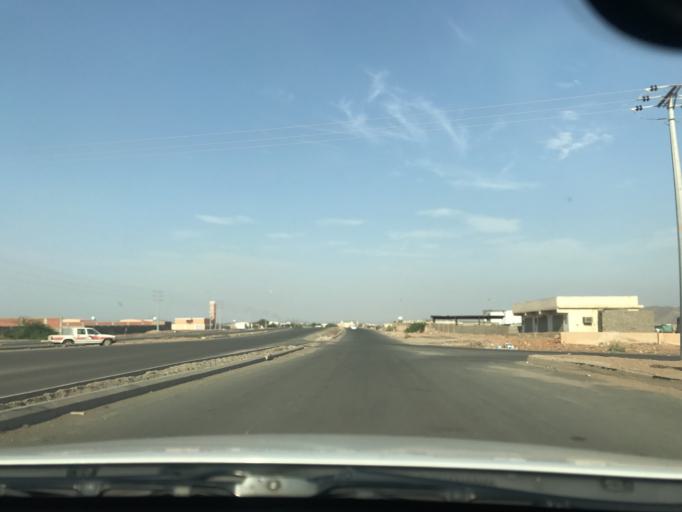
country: SA
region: Makkah
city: Al Jumum
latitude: 21.4537
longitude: 39.5390
